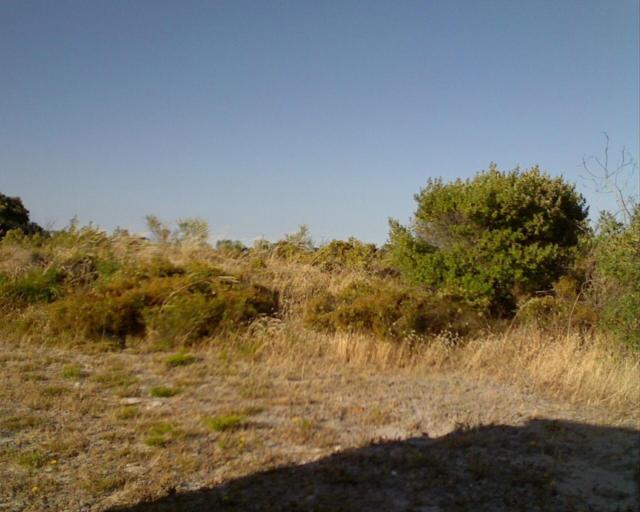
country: AU
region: Western Australia
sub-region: Dandaragan
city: Jurien Bay
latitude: -30.0511
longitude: 114.9752
